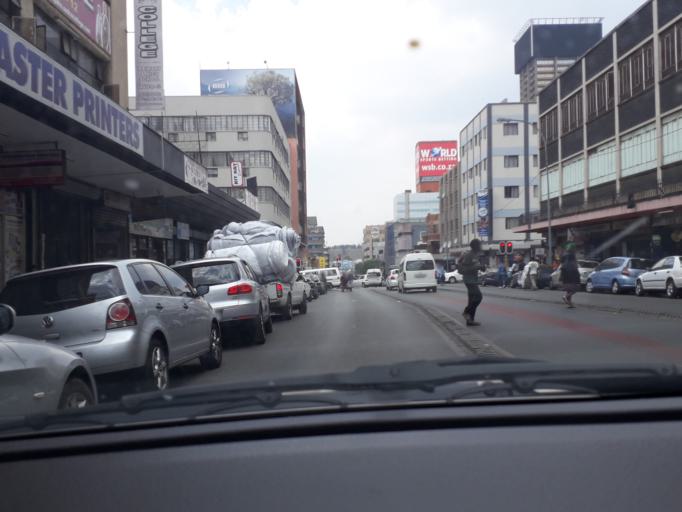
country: ZA
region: Gauteng
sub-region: City of Johannesburg Metropolitan Municipality
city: Johannesburg
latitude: -26.2023
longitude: 28.0506
